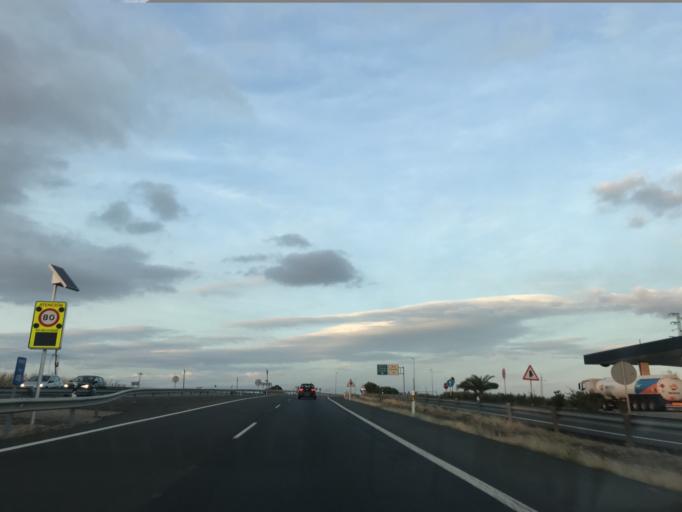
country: ES
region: Andalusia
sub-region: Province of Cordoba
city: La Victoria
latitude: 37.7579
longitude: -4.8288
